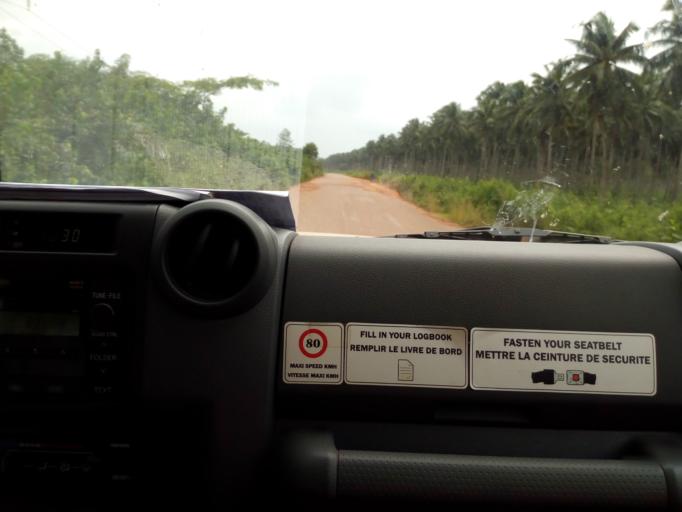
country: CI
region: Bas-Sassandra
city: Tabou
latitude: 4.5300
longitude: -7.2335
